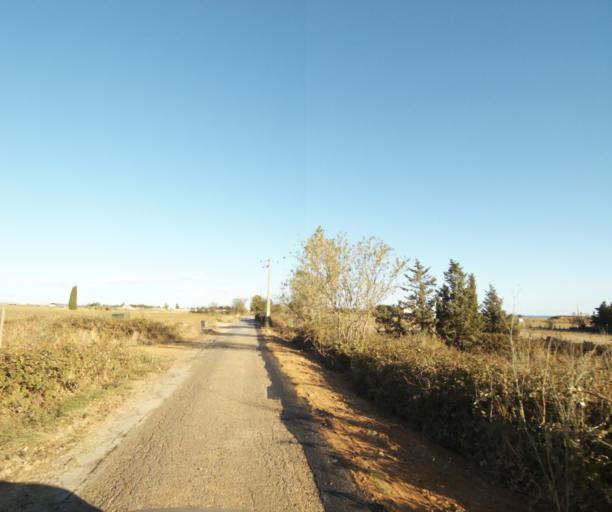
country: FR
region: Languedoc-Roussillon
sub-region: Departement du Gard
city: Bouillargues
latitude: 43.7847
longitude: 4.4521
